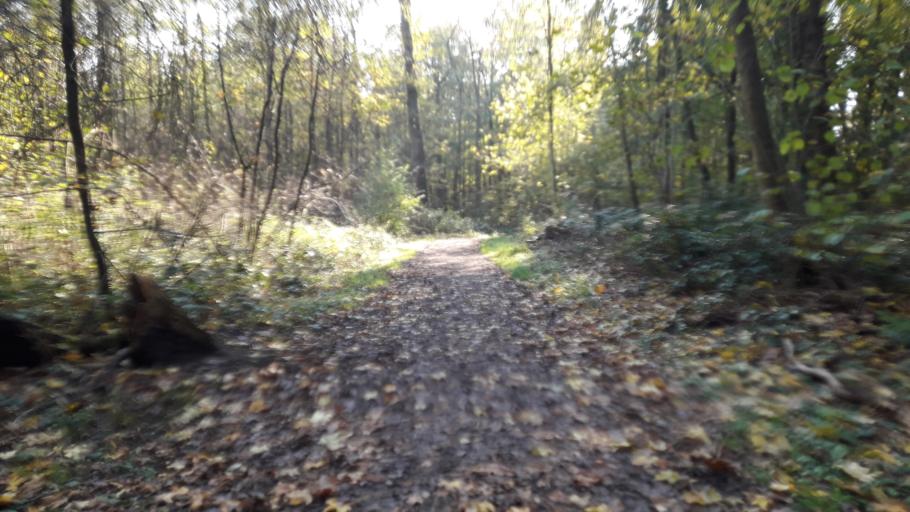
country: DE
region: North Rhine-Westphalia
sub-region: Regierungsbezirk Detmold
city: Paderborn
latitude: 51.7567
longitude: 8.7073
